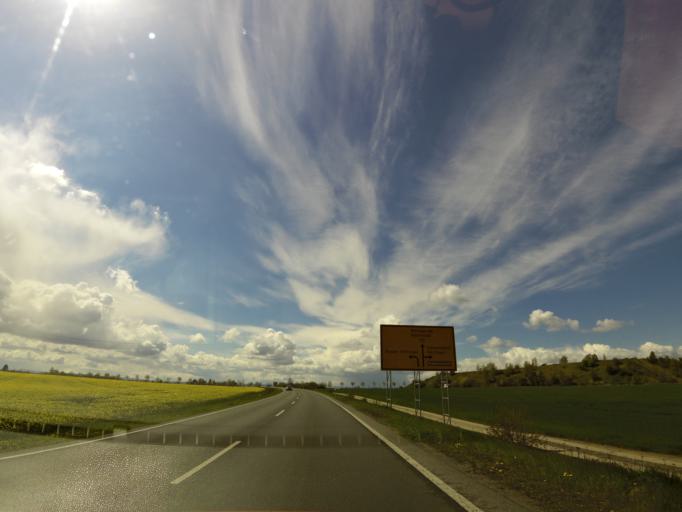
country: DE
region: Saxony-Anhalt
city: Groeningen
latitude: 51.9446
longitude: 11.1939
